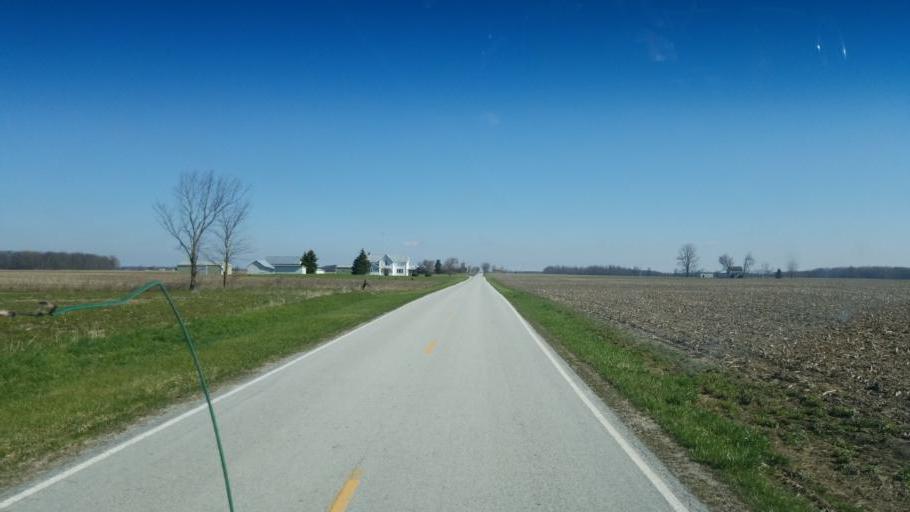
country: US
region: Ohio
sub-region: Hardin County
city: Forest
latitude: 40.7047
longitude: -83.4958
